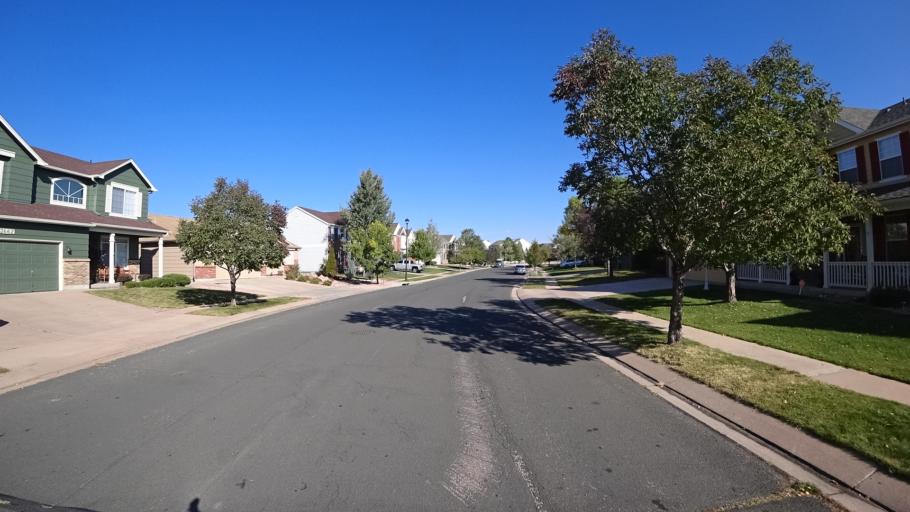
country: US
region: Colorado
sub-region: El Paso County
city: Cimarron Hills
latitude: 38.8836
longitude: -104.7087
